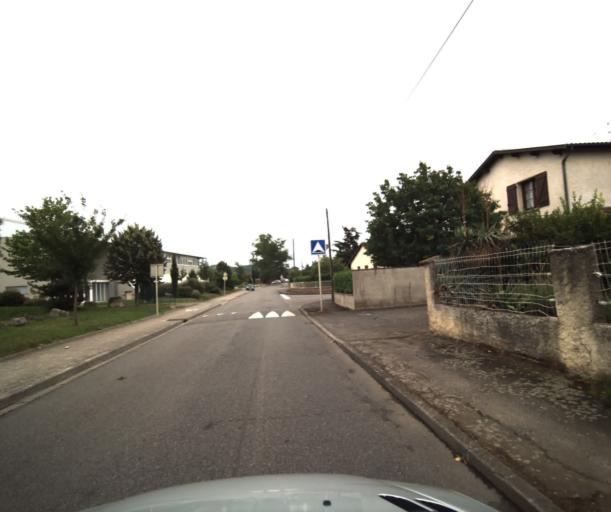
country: FR
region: Midi-Pyrenees
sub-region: Departement de la Haute-Garonne
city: Pinsaguel
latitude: 43.5052
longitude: 1.3934
